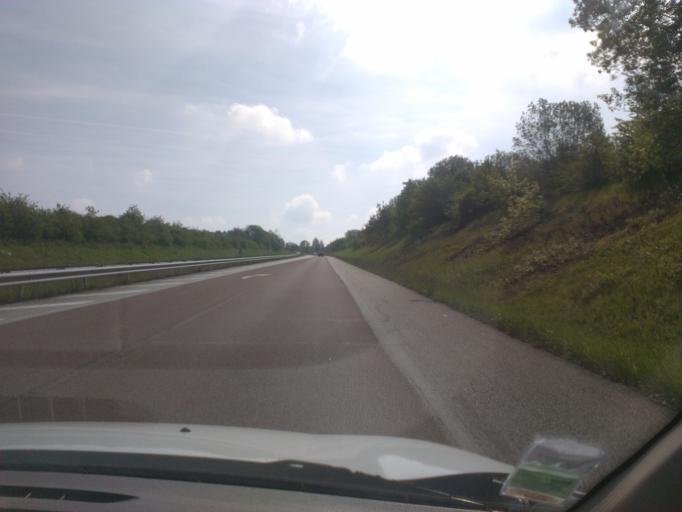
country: FR
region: Lorraine
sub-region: Departement des Vosges
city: Uxegney
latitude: 48.2050
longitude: 6.3807
